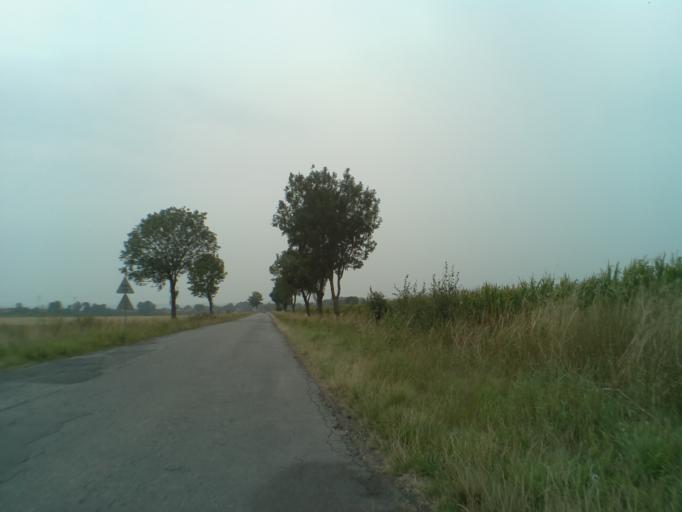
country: PL
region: Lower Silesian Voivodeship
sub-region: Powiat swidnicki
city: Swiebodzice
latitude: 50.9118
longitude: 16.3204
